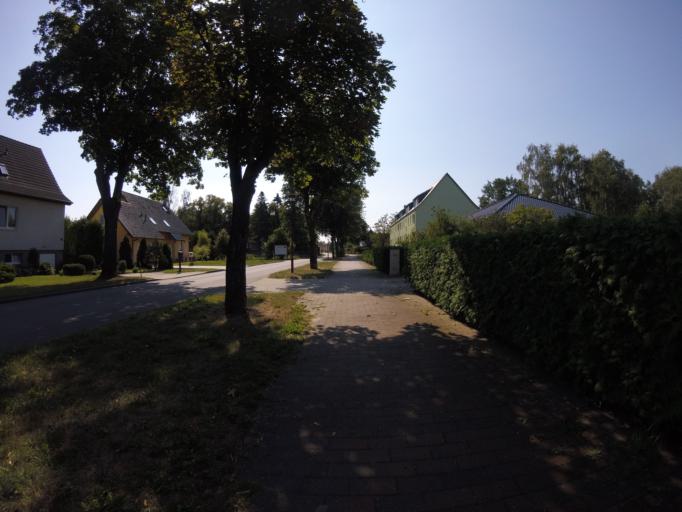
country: DE
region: Brandenburg
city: Mullrose
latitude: 52.2455
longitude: 14.4083
